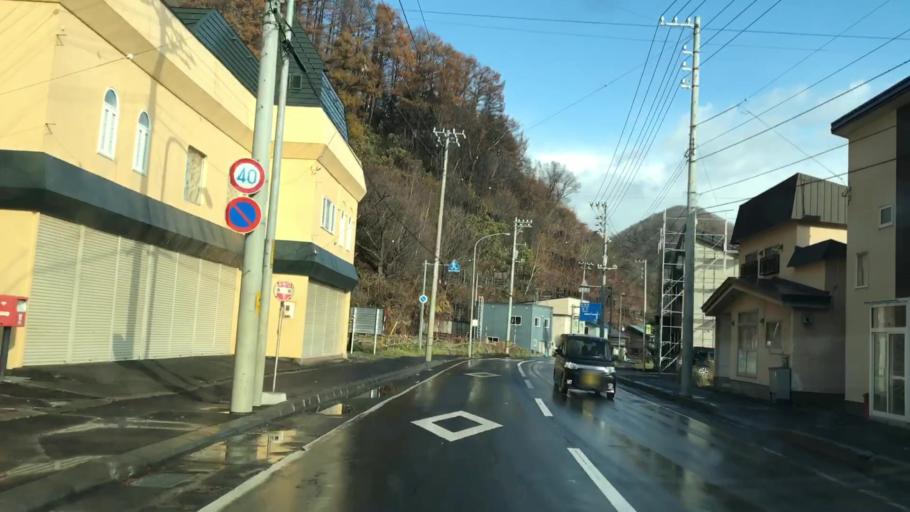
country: JP
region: Hokkaido
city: Yoichi
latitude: 43.2745
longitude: 140.6354
